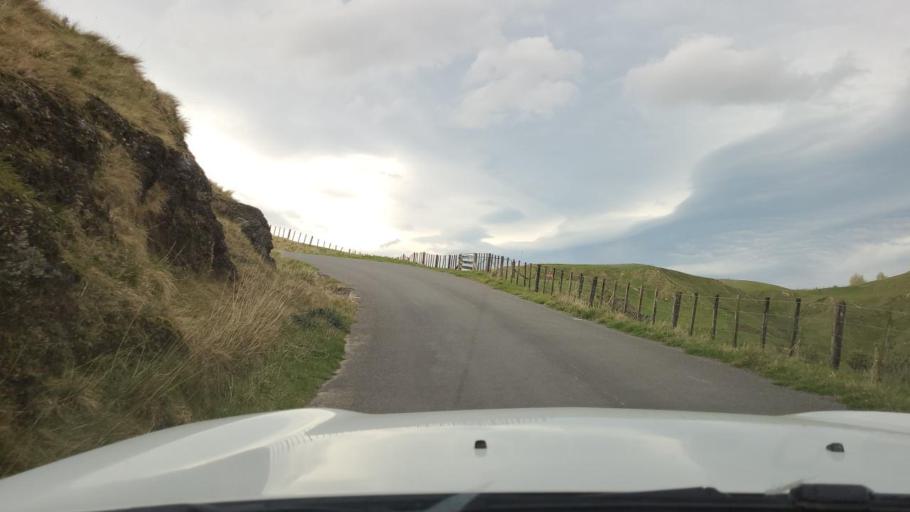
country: NZ
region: Hawke's Bay
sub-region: Napier City
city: Napier
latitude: -39.2026
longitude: 176.9466
